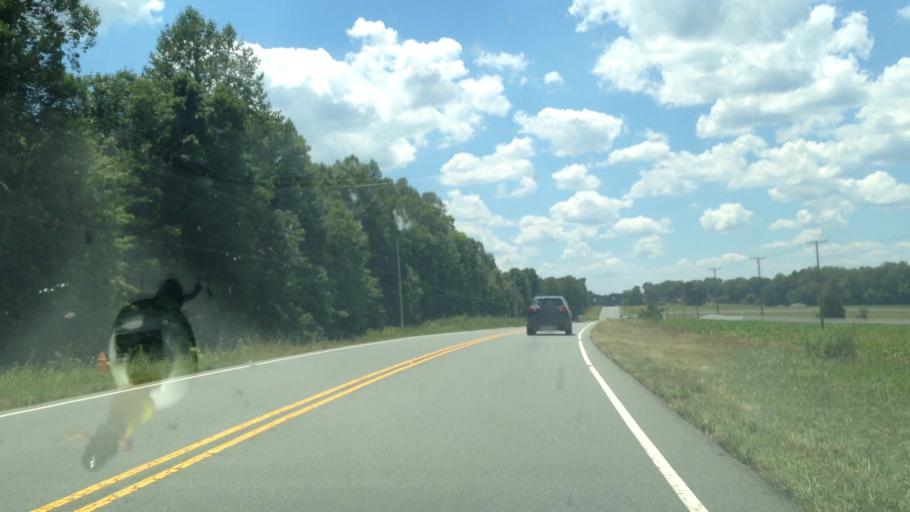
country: US
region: North Carolina
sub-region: Forsyth County
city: Walkertown
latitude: 36.1961
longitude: -80.0938
